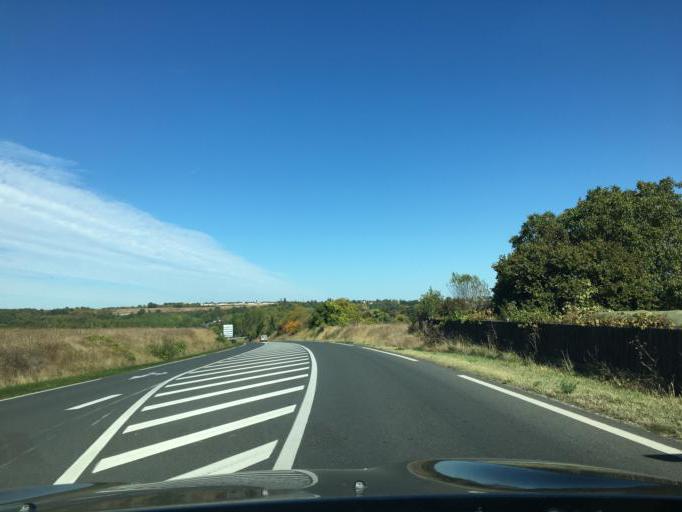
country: FR
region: Centre
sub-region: Departement d'Indre-et-Loire
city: Azay-le-Rideau
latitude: 47.2521
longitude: 0.4537
